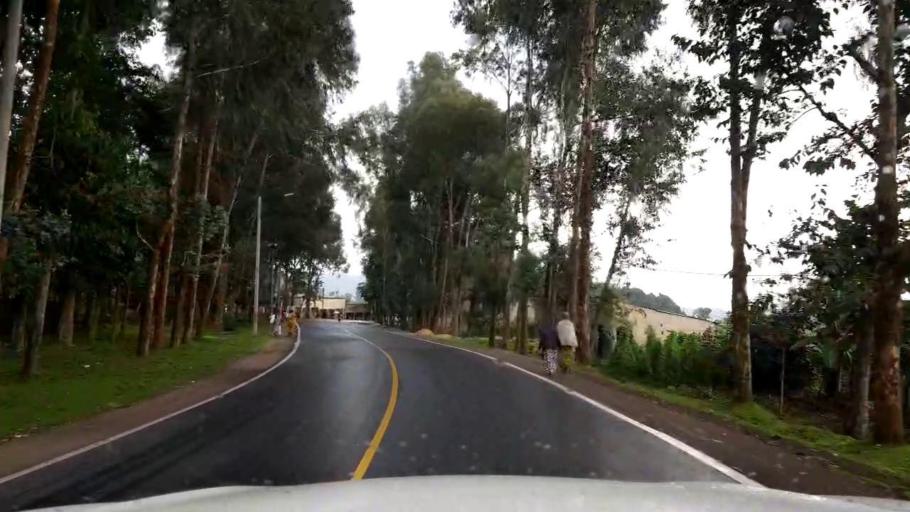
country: RW
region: Western Province
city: Gisenyi
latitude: -1.6760
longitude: 29.3558
